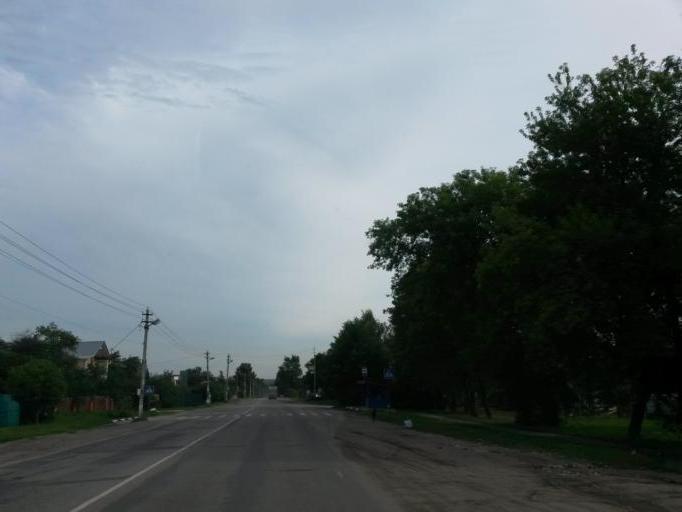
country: RU
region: Moskovskaya
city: Yam
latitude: 55.4774
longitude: 37.7526
